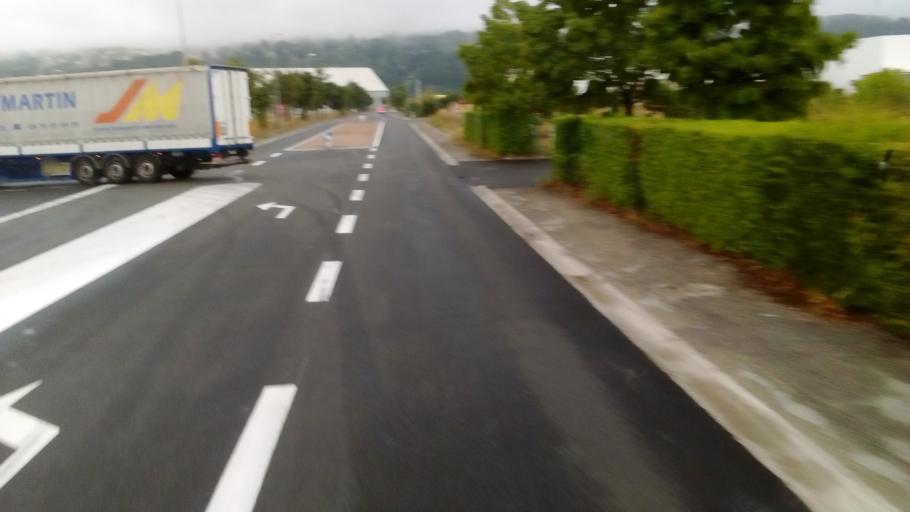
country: FR
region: Rhone-Alpes
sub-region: Departement de l'Ardeche
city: Soyons
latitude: 44.8936
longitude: 4.8657
